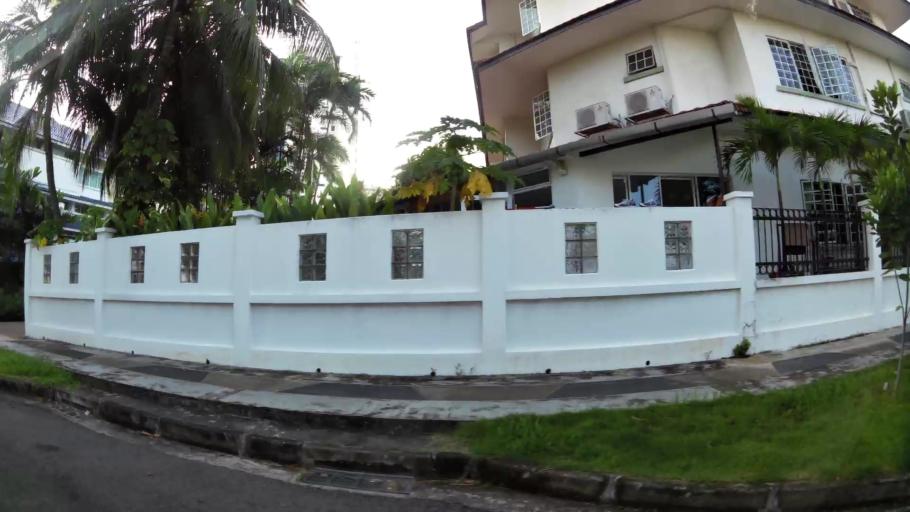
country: SG
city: Singapore
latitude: 1.3100
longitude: 103.9238
